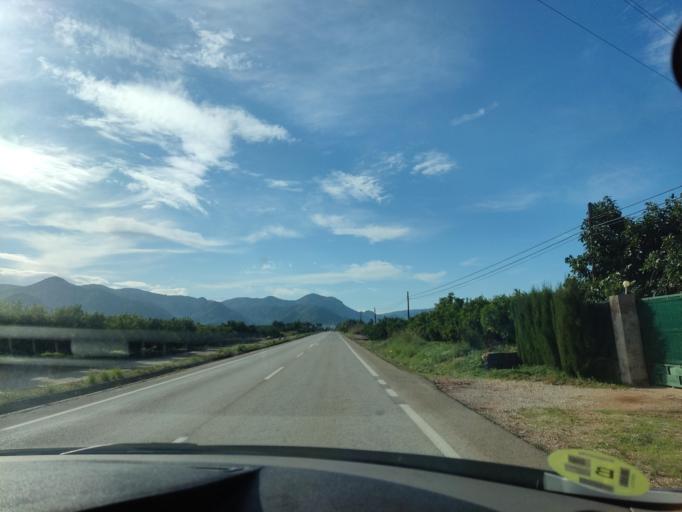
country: ES
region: Valencia
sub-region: Provincia de Alicante
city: Pego
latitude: 38.8474
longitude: -0.0840
